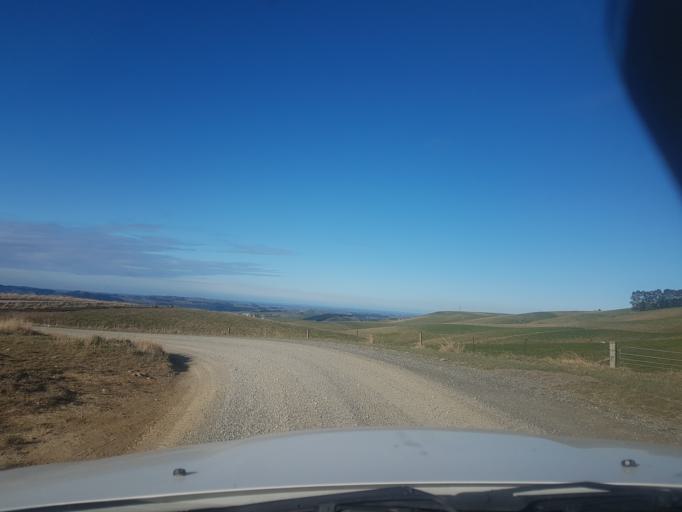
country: NZ
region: Canterbury
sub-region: Timaru District
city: Pleasant Point
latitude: -44.1672
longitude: 170.9020
